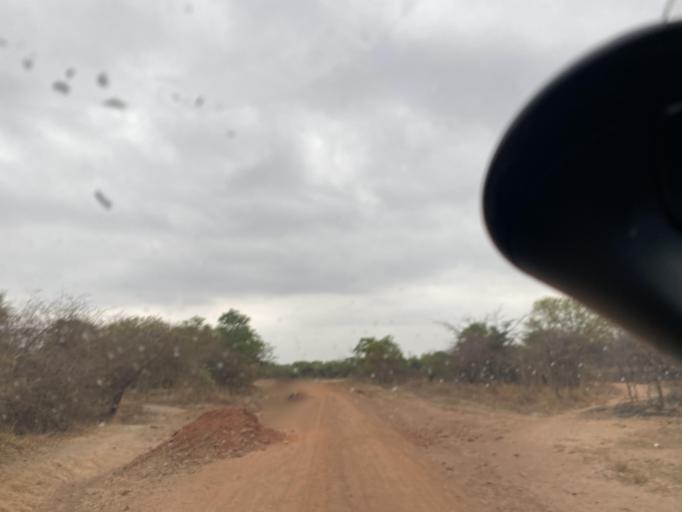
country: ZM
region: Lusaka
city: Chongwe
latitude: -15.1619
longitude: 28.7582
